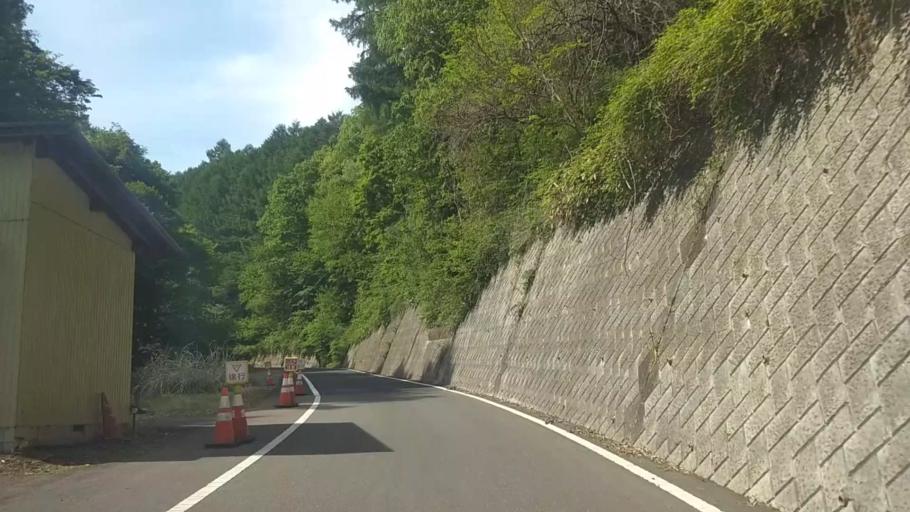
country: JP
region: Nagano
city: Saku
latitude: 36.1131
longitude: 138.4709
